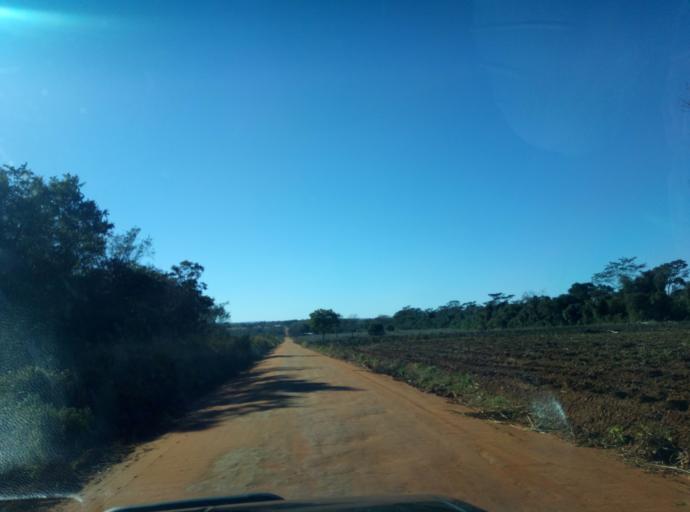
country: PY
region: Caaguazu
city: Doctor Cecilio Baez
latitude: -25.1622
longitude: -56.2690
